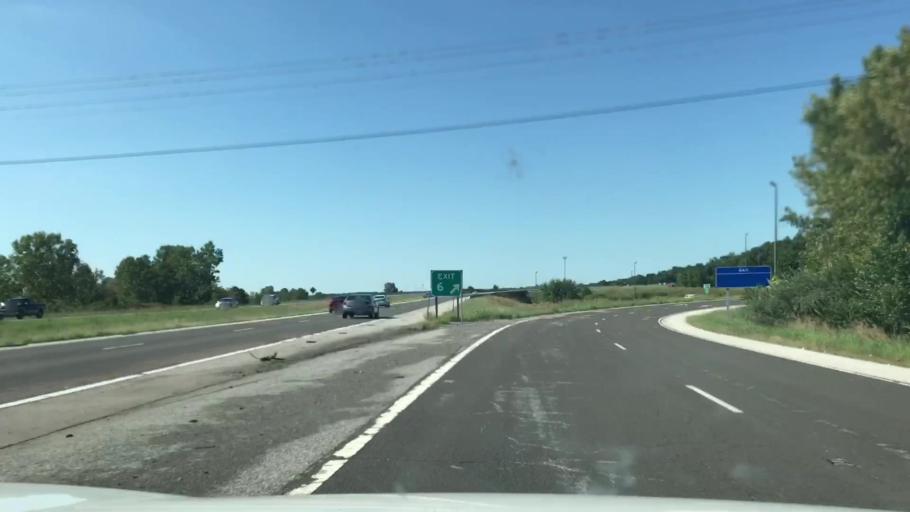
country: US
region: Illinois
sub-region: Madison County
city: South Roxana
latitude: 38.8473
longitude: -90.0491
